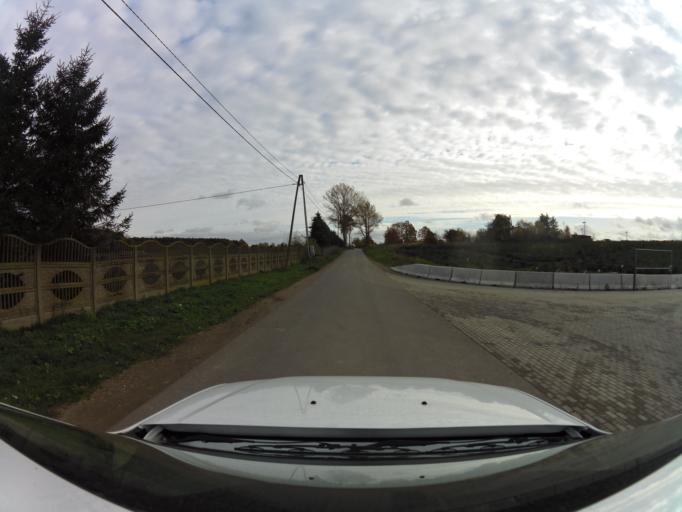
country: PL
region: West Pomeranian Voivodeship
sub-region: Powiat gryficki
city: Cerkwica
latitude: 54.0430
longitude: 15.1274
